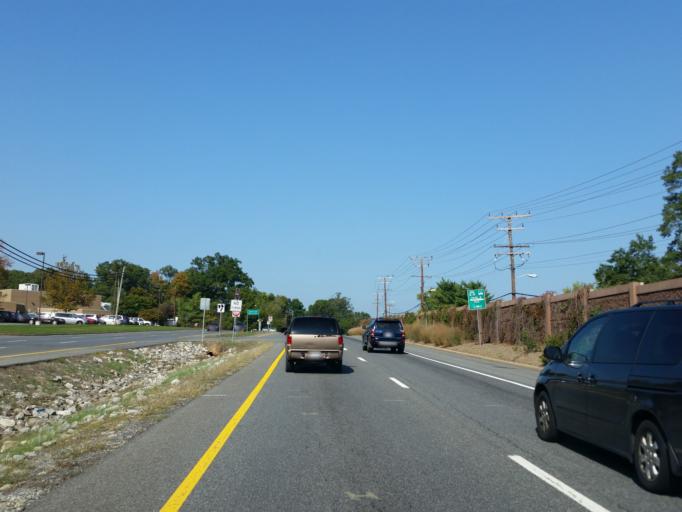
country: US
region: Maryland
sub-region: Prince George's County
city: South Laurel
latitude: 39.0710
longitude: -76.8444
